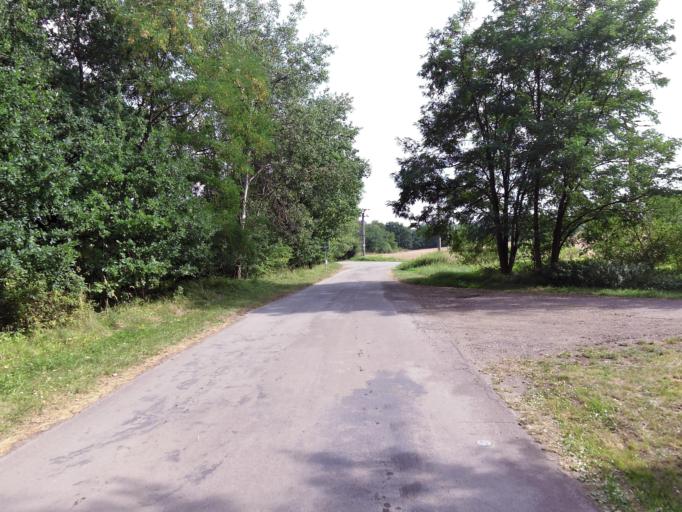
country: CZ
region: Central Bohemia
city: Kamenny Privoz
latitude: 49.8534
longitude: 14.5468
